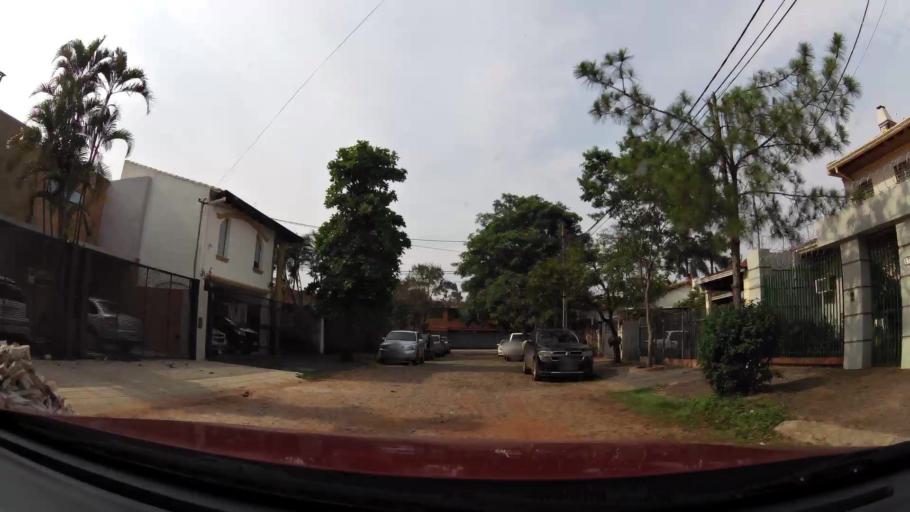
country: PY
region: Central
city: Fernando de la Mora
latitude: -25.2847
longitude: -57.5584
